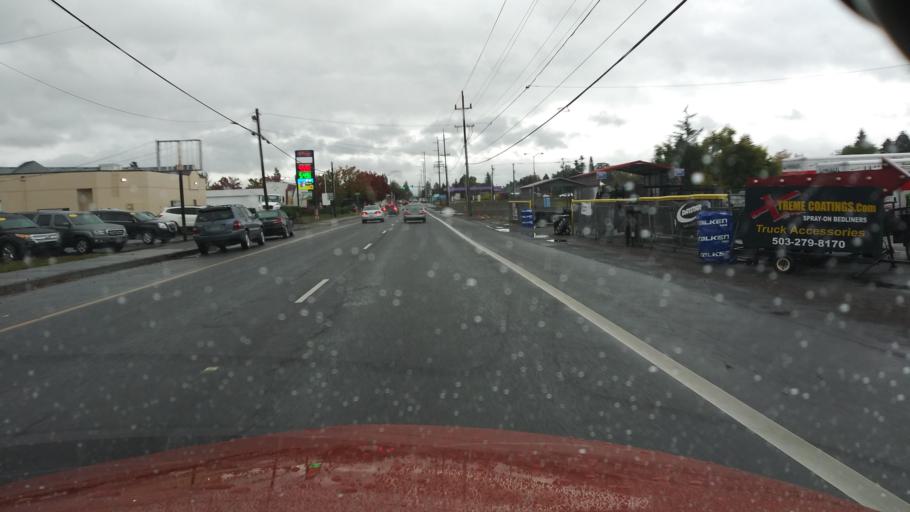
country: US
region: Oregon
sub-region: Washington County
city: Cornelius
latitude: 45.5200
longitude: -123.0627
